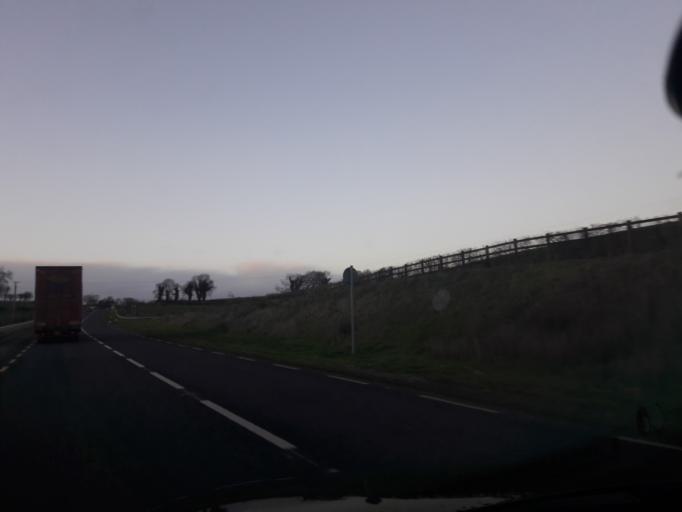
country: IE
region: Ulster
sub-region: County Monaghan
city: Monaghan
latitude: 54.2821
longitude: -6.9642
